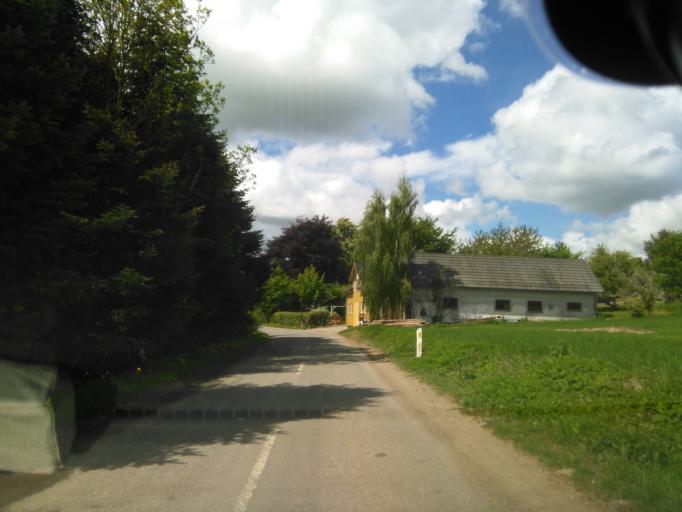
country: DK
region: Central Jutland
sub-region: Arhus Kommune
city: Solbjerg
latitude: 56.0259
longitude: 10.1134
